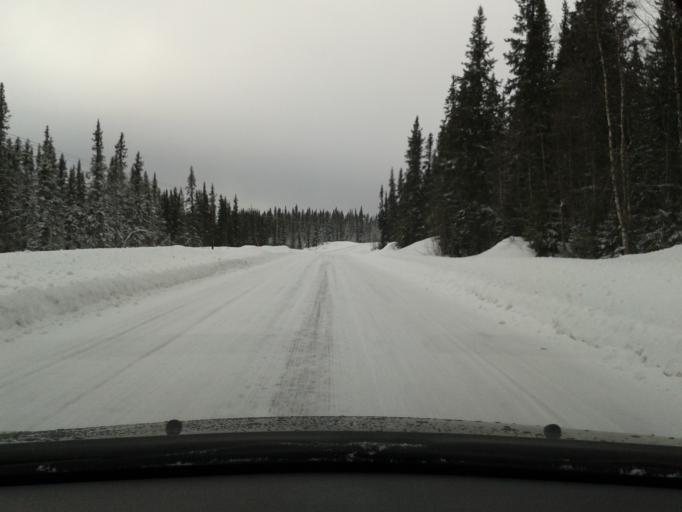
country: SE
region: Vaesterbotten
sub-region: Vilhelmina Kommun
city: Sjoberg
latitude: 65.1899
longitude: 15.9456
